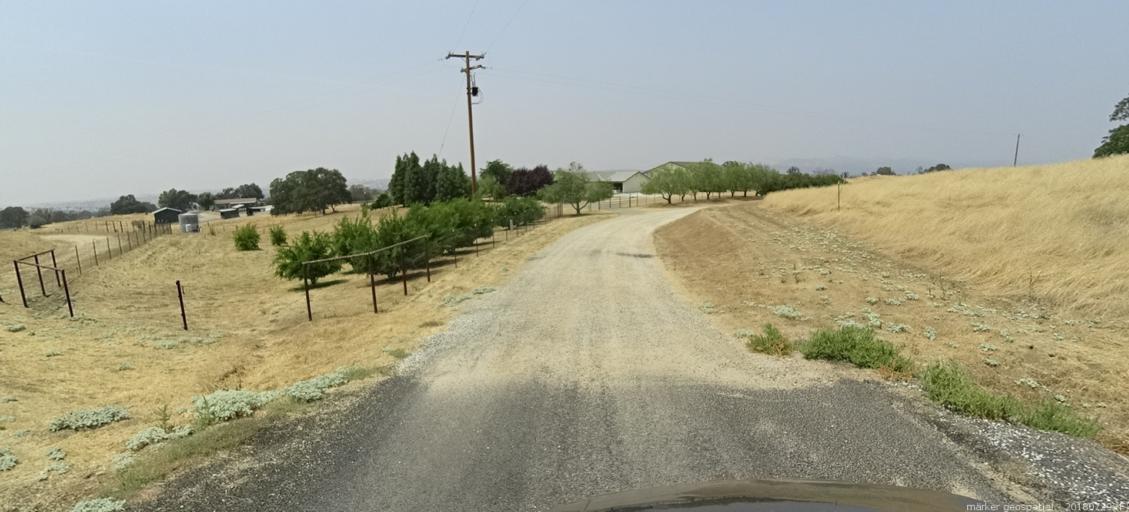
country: US
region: California
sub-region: Madera County
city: Yosemite Lakes
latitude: 37.2393
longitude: -119.9141
